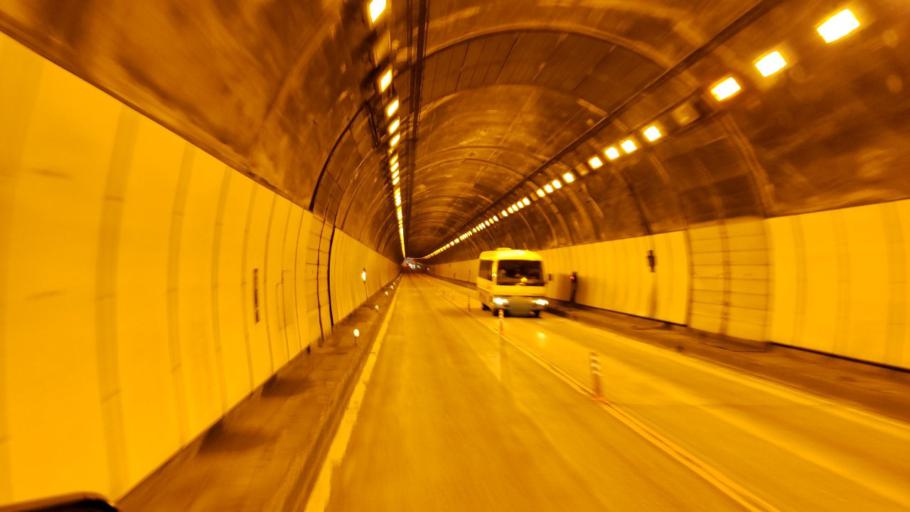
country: JP
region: Hyogo
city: Himeji
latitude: 34.9701
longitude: 134.7690
